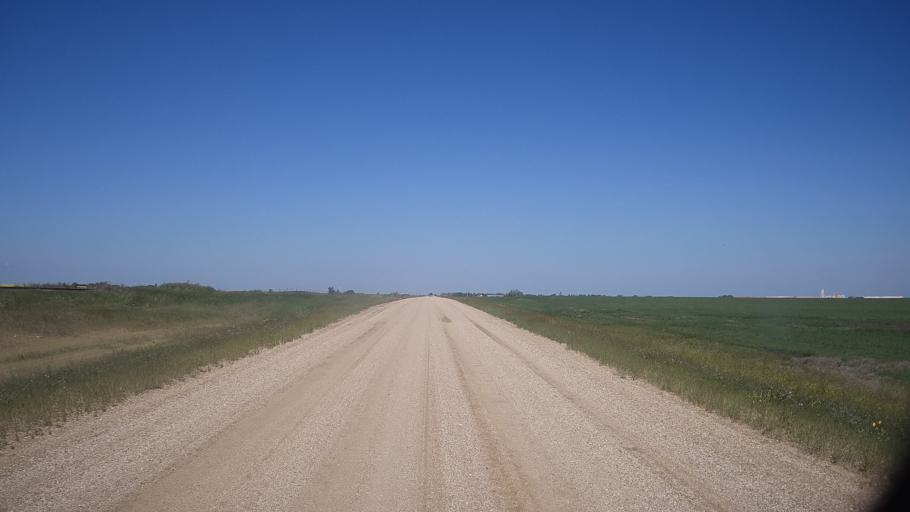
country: CA
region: Saskatchewan
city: Watrous
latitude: 51.8789
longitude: -106.0165
